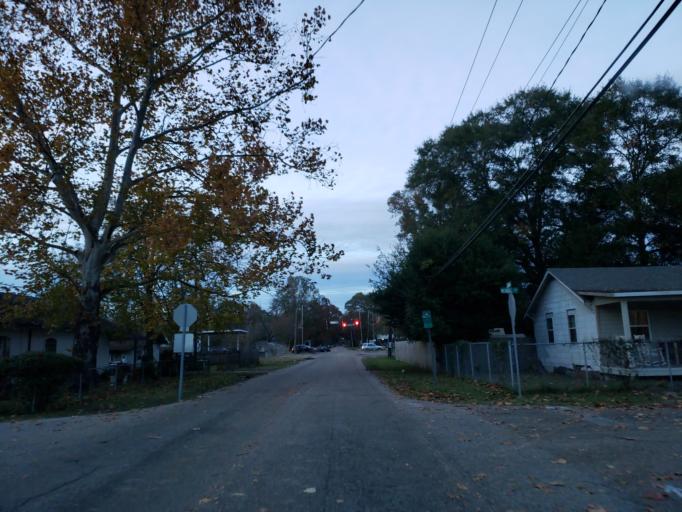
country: US
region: Mississippi
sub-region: Forrest County
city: Hattiesburg
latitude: 31.3241
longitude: -89.2801
